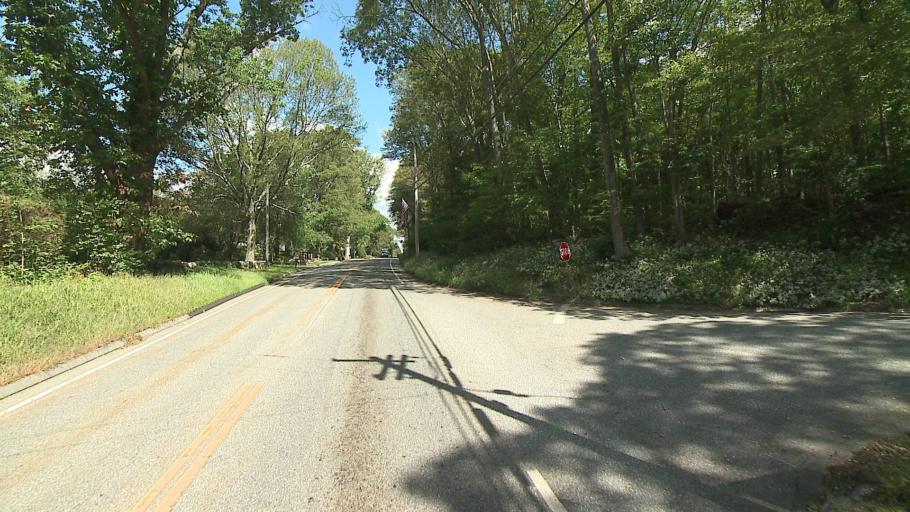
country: US
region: Connecticut
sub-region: Windham County
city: South Woodstock
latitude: 41.8779
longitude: -71.9617
